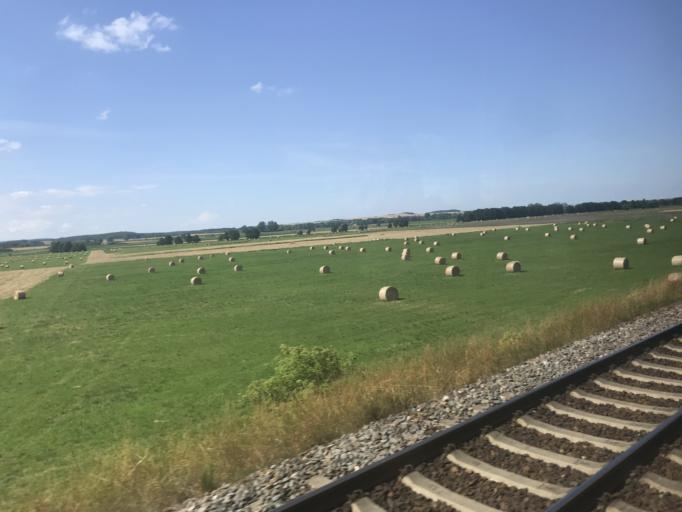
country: DE
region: Brandenburg
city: Pinnow
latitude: 53.0950
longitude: 14.0176
